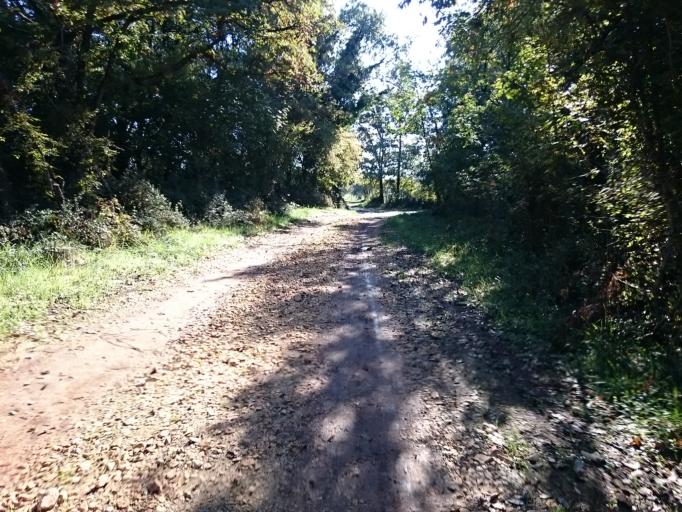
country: HR
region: Istarska
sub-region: Grad Porec
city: Porec
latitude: 45.2697
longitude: 13.5805
